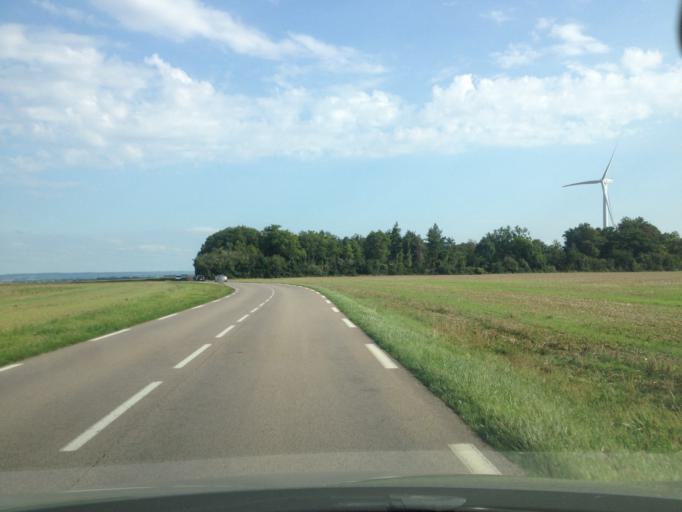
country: FR
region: Lower Normandy
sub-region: Departement du Calvados
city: Moult
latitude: 49.0800
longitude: -0.1447
